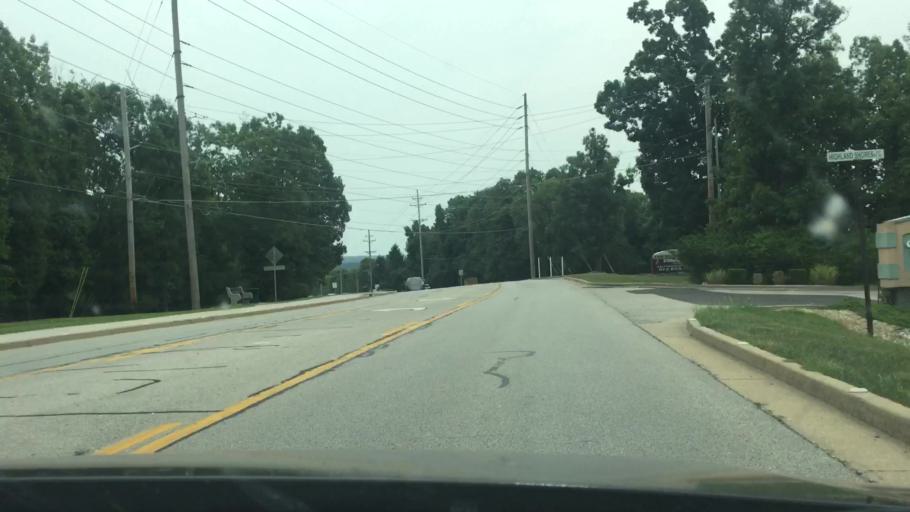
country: US
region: Missouri
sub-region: Miller County
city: Lake Ozark
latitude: 38.1942
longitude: -92.6735
